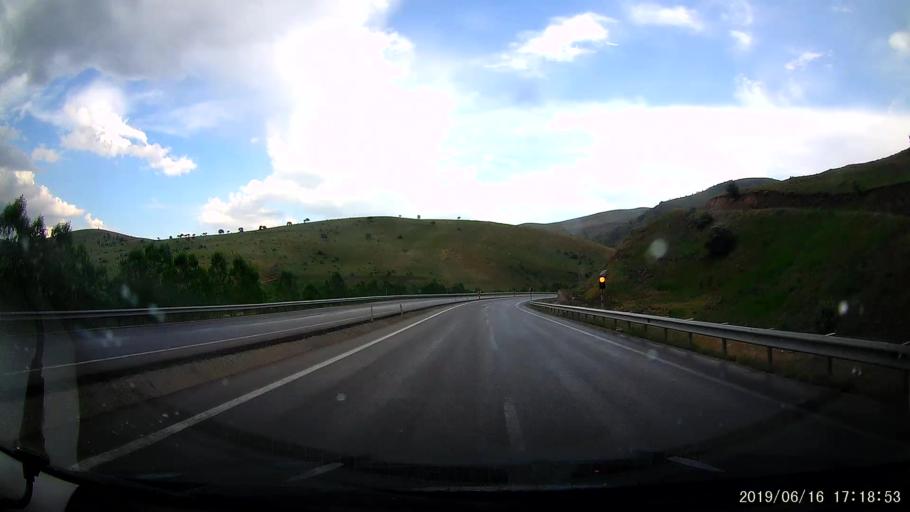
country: TR
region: Erzincan
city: Tercan
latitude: 39.8079
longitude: 40.5306
